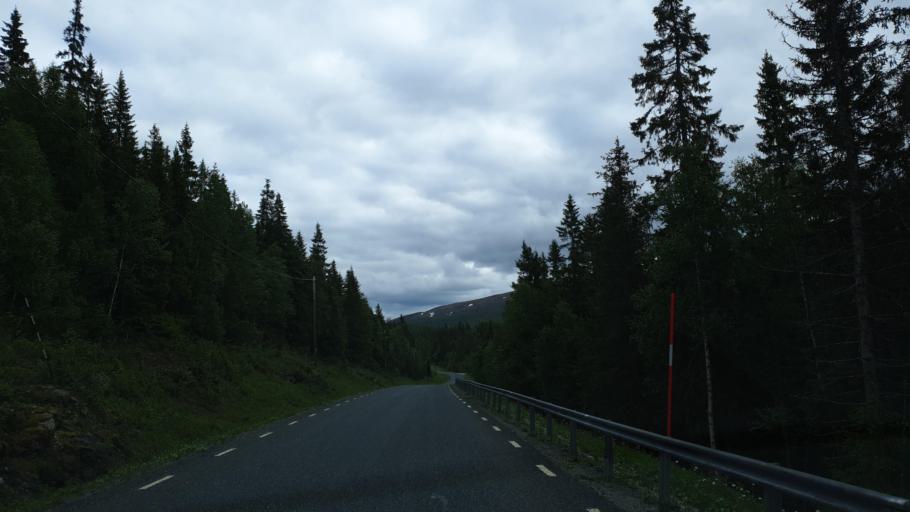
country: NO
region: Nordland
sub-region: Hattfjelldal
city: Hattfjelldal
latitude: 65.4347
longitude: 14.5781
